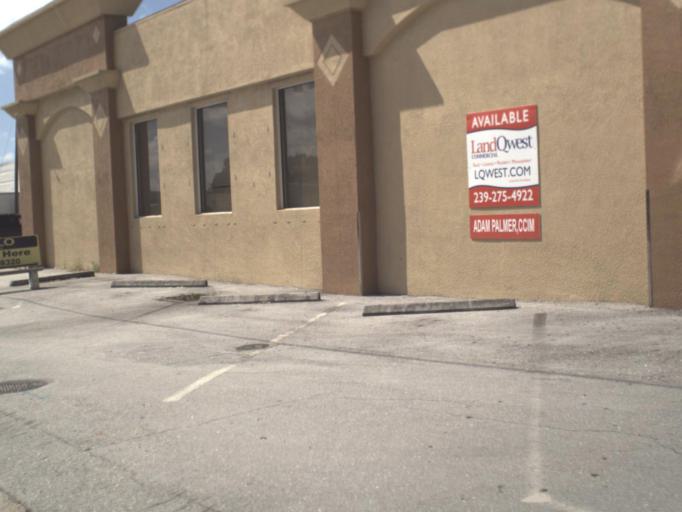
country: US
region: Florida
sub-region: Lee County
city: North Fort Myers
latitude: 26.6361
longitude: -81.8727
